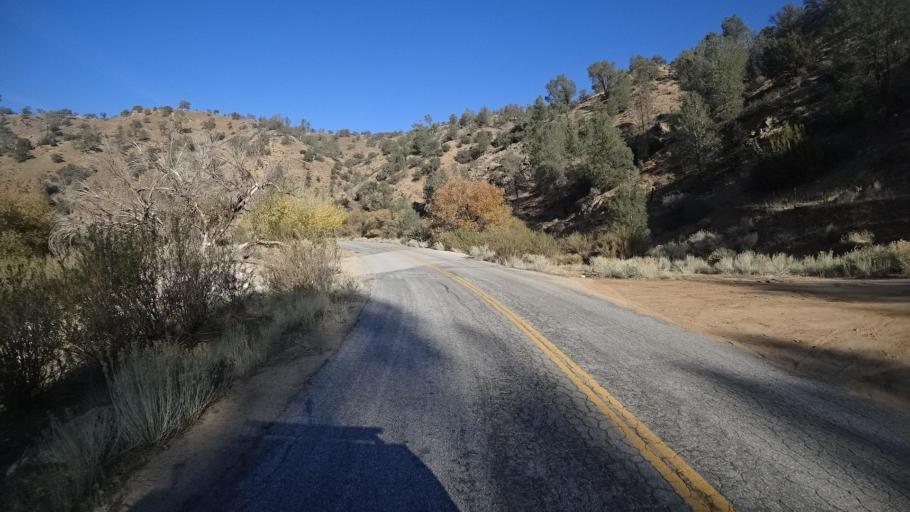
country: US
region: California
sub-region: Kern County
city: Golden Hills
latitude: 35.3057
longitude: -118.4510
